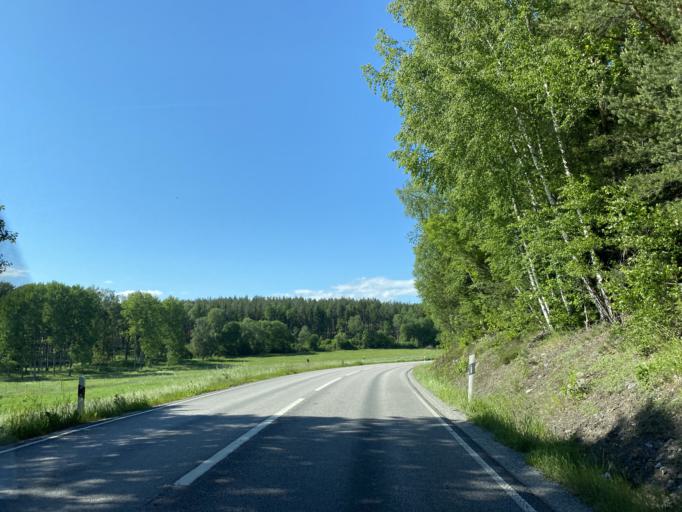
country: SE
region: Stockholm
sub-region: Norrtalje Kommun
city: Norrtalje
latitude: 59.8025
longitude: 18.6516
